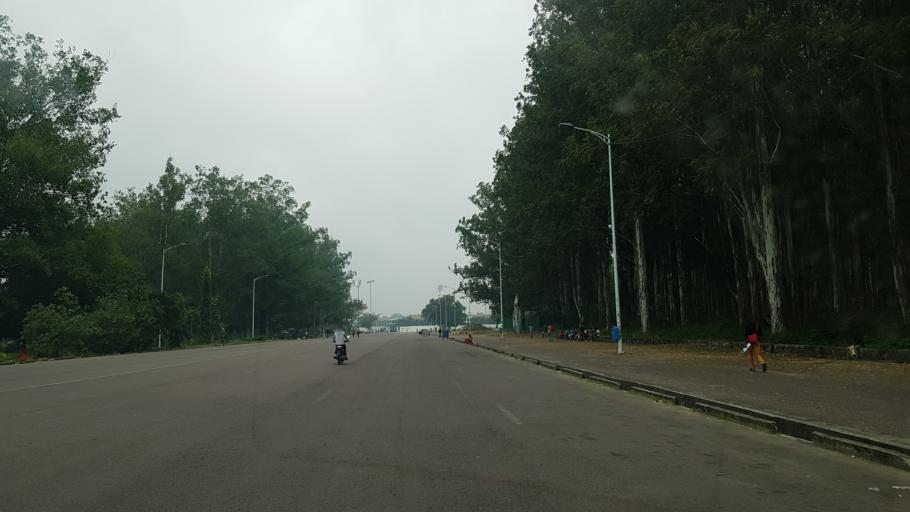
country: CG
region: Brazzaville
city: Brazzaville
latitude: -4.2701
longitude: 15.2539
